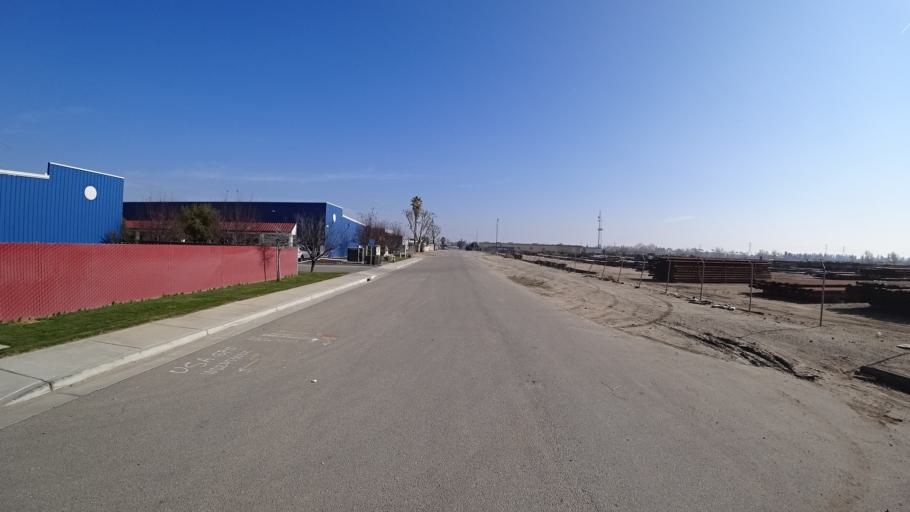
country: US
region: California
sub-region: Kern County
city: Bakersfield
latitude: 35.3788
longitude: -119.0564
